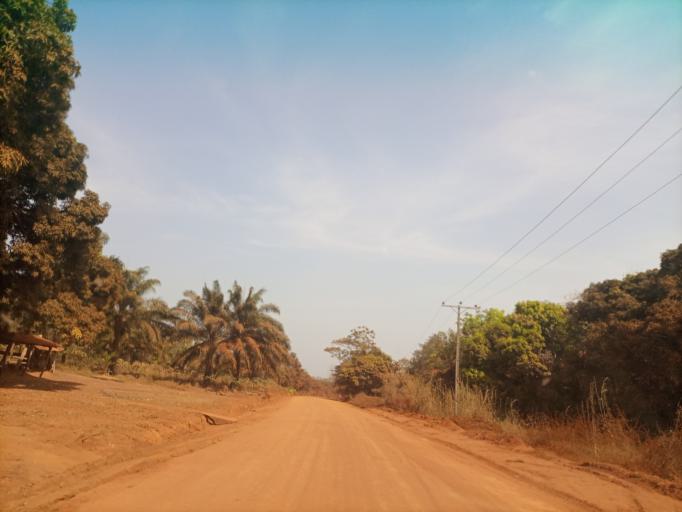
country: NG
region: Enugu
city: Eha Amufu
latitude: 6.6742
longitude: 7.7290
